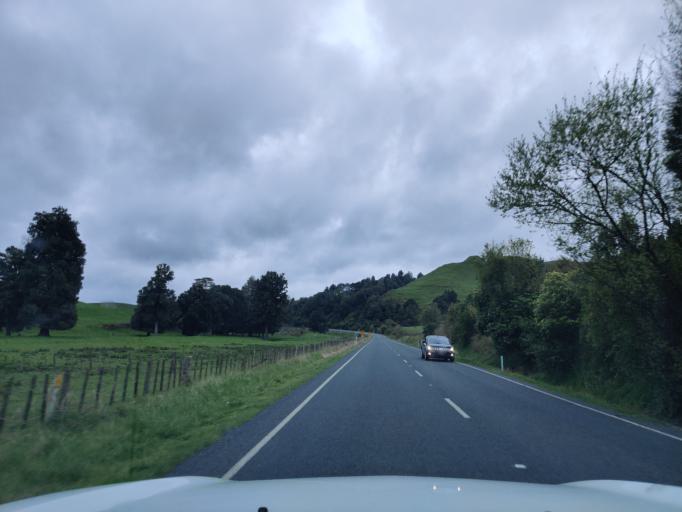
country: NZ
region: Waikato
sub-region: Otorohanga District
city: Otorohanga
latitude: -38.5454
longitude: 175.1844
